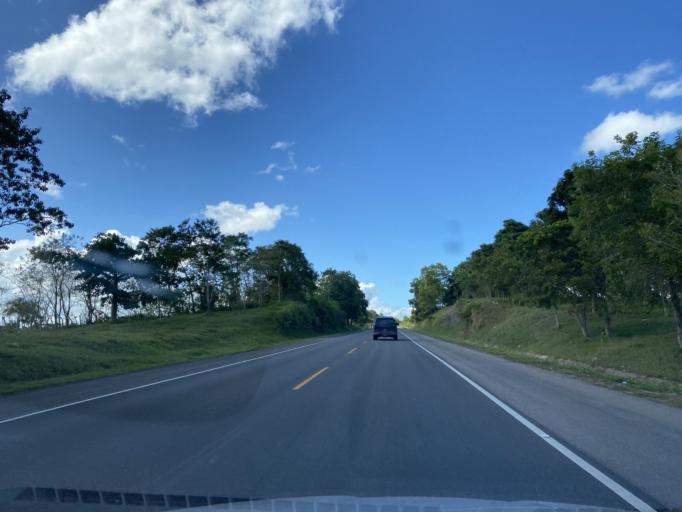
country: DO
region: Monte Plata
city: Sabana Grande de Boya
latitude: 18.9767
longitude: -69.7936
